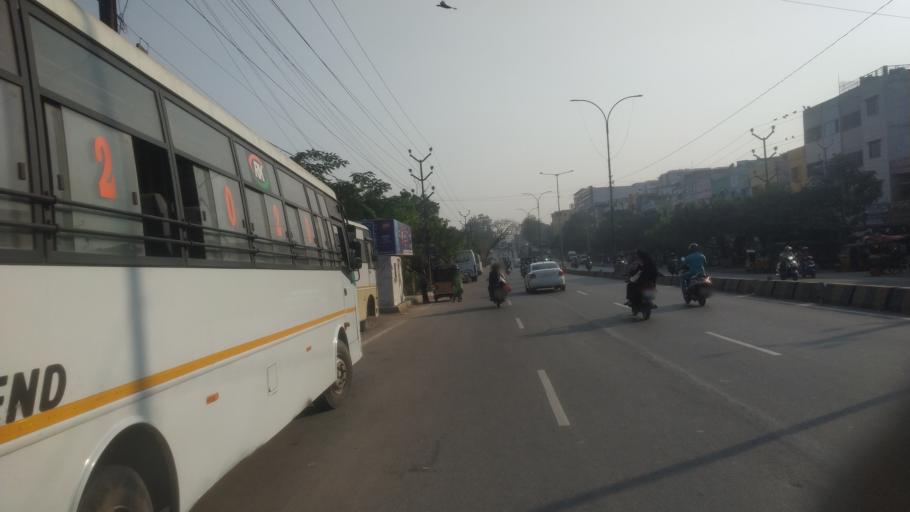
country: IN
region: Telangana
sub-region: Rangareddi
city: Quthbullapur
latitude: 17.4861
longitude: 78.4500
